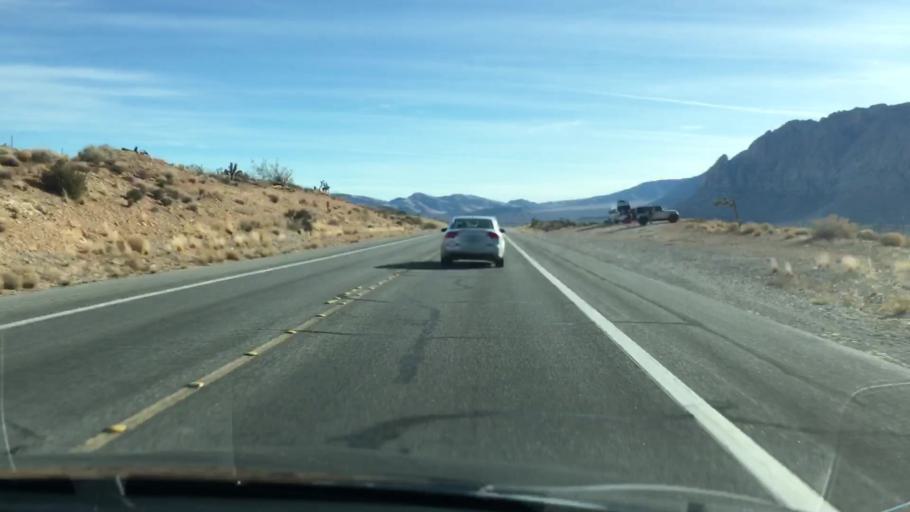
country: US
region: Nevada
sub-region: Clark County
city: Summerlin South
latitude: 36.1009
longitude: -115.4488
